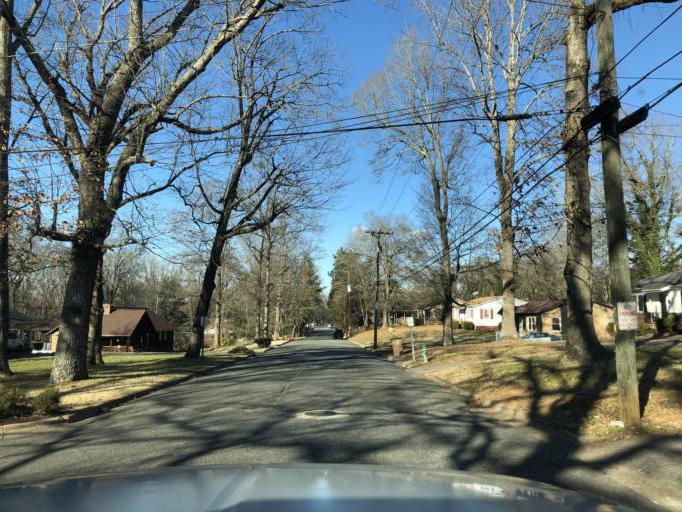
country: US
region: North Carolina
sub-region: Cleveland County
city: Shelby
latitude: 35.3024
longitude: -81.5414
